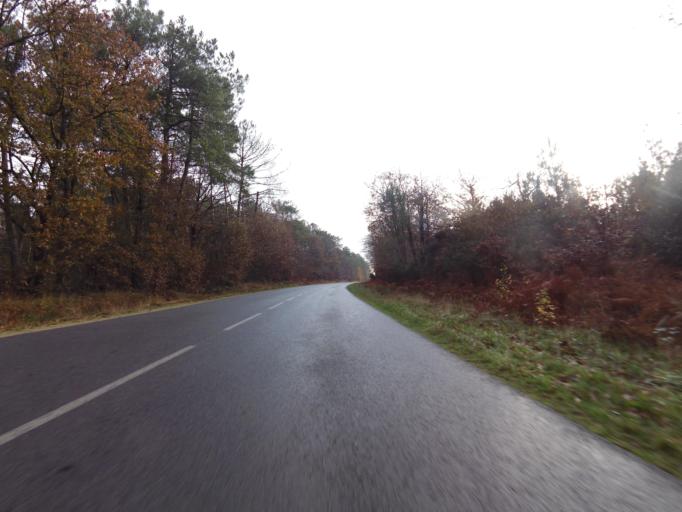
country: FR
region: Brittany
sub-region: Departement du Morbihan
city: Saint-Martin-sur-Oust
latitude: 47.7254
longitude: -2.2672
